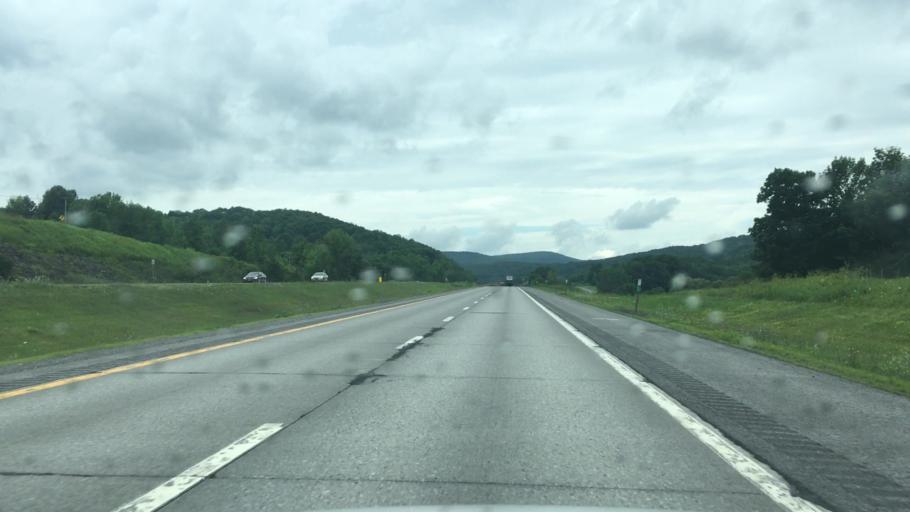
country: US
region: New York
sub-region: Schoharie County
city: Cobleskill
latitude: 42.6427
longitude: -74.5834
